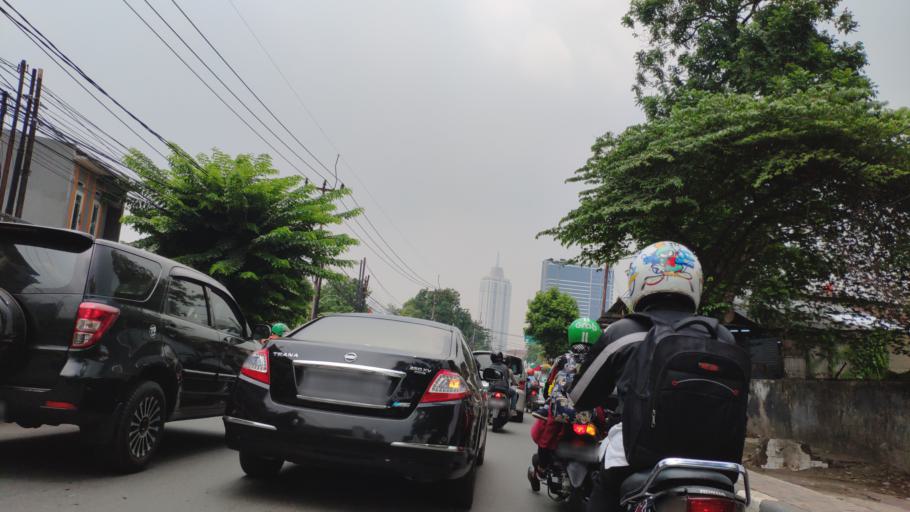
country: ID
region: Banten
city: South Tangerang
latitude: -6.2477
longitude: 106.7786
